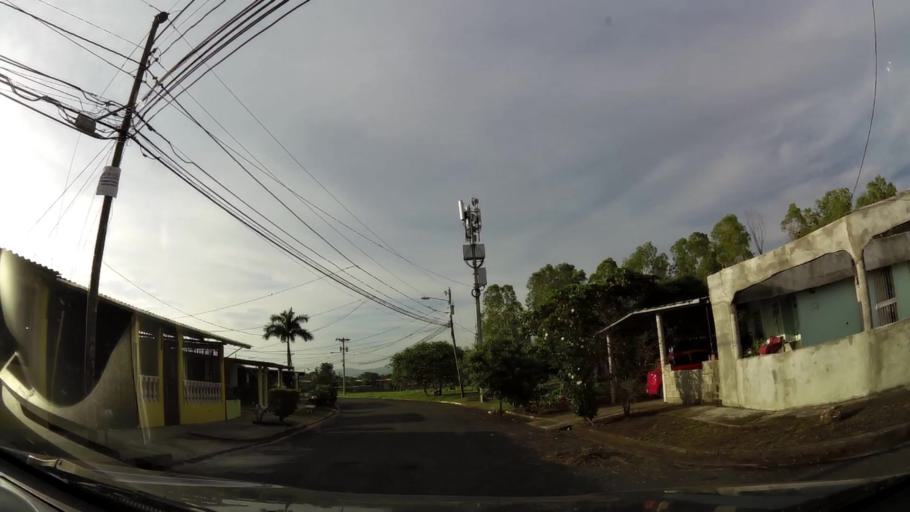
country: PA
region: Panama
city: Cabra Numero Uno
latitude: 9.0823
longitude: -79.3529
